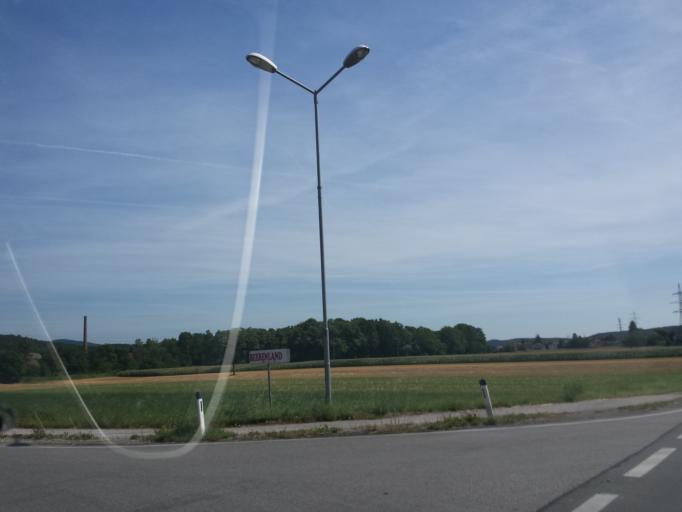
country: AT
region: Lower Austria
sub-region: Politischer Bezirk Neunkirchen
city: Enzenreith
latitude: 47.6739
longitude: 15.9676
